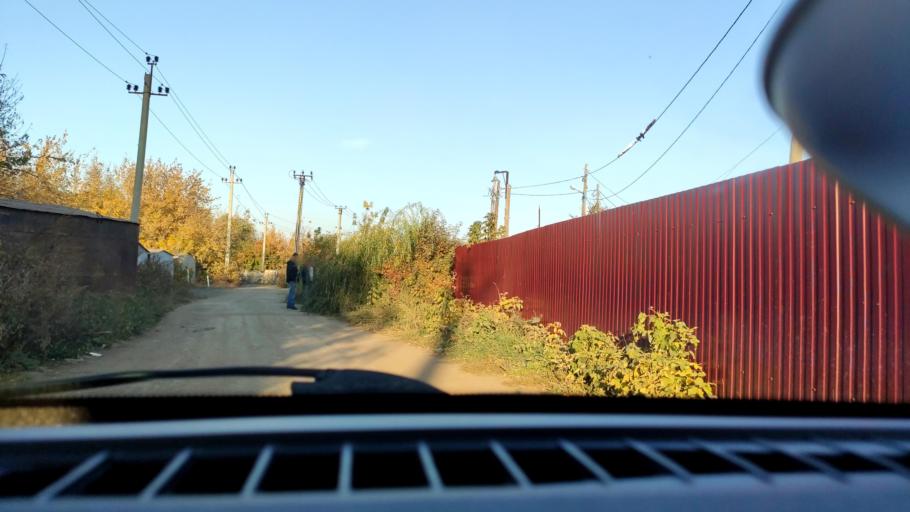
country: RU
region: Samara
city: Samara
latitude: 53.1818
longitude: 50.2237
